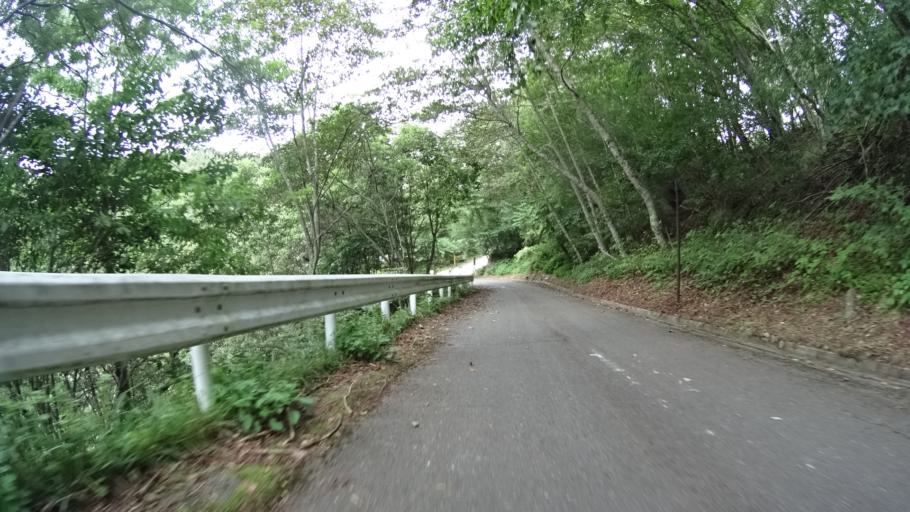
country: JP
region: Yamanashi
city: Nirasaki
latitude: 35.8062
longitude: 138.5291
